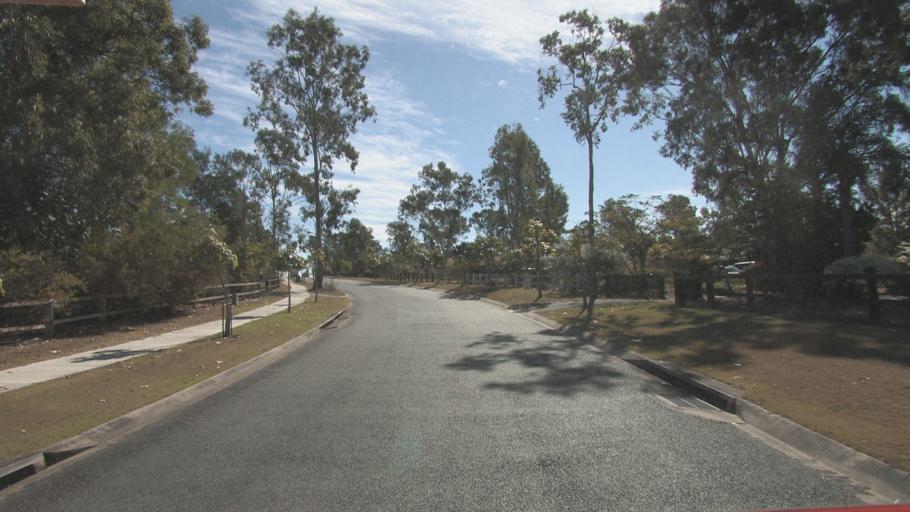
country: AU
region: Queensland
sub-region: Logan
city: North Maclean
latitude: -27.8086
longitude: 152.9625
